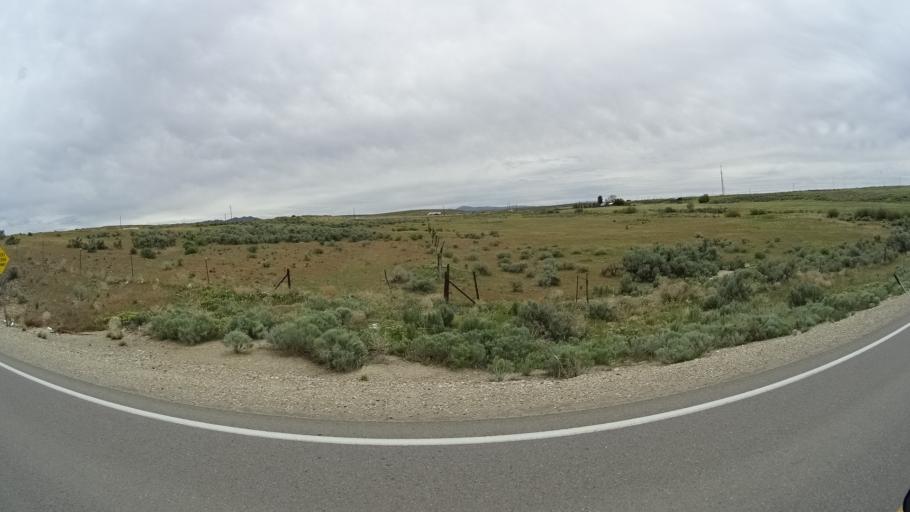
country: US
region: Idaho
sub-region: Ada County
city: Boise
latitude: 43.4601
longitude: -116.0949
